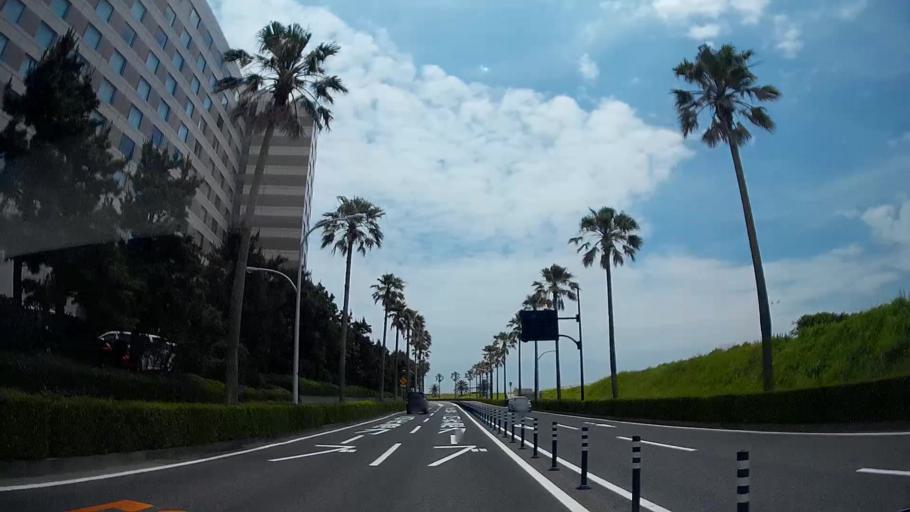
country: JP
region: Tokyo
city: Urayasu
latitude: 35.6281
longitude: 139.8731
